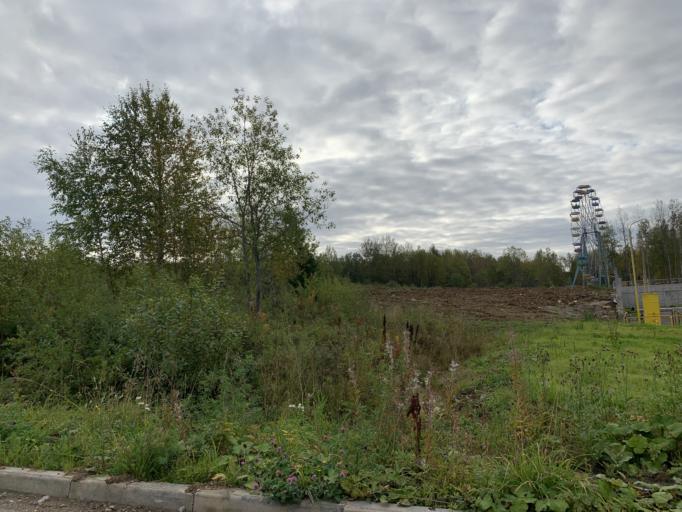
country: RU
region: Perm
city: Gubakha
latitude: 58.8347
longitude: 57.5624
